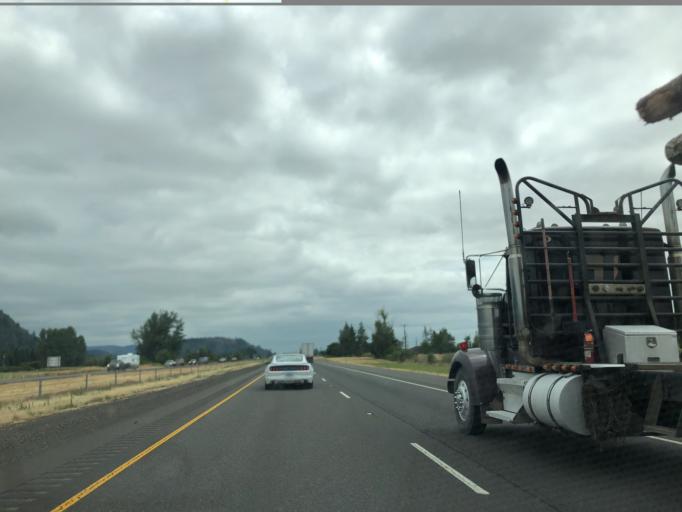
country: US
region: Oregon
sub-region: Lane County
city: Coburg
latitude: 44.2179
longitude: -123.0609
